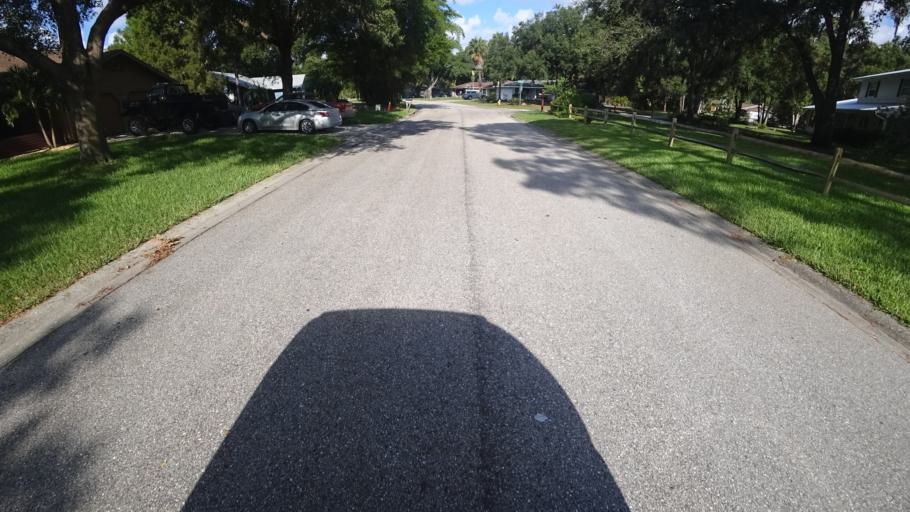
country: US
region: Florida
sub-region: Sarasota County
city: Desoto Lakes
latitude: 27.4322
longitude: -82.4522
